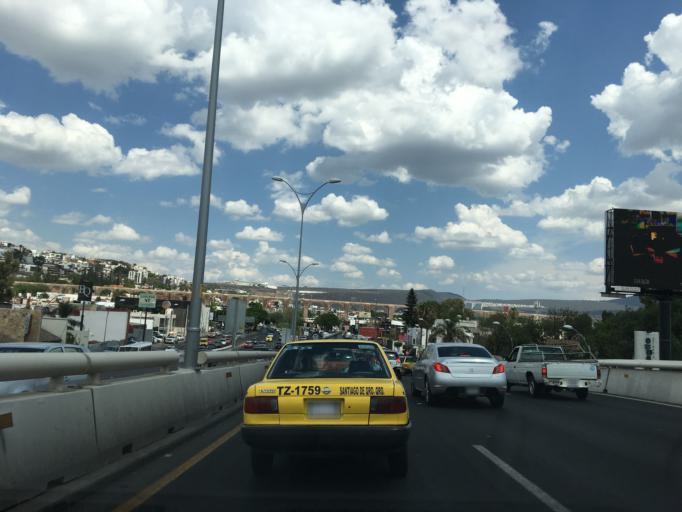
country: MX
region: Queretaro
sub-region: Queretaro
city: Santiago de Queretaro
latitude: 20.5997
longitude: -100.3754
